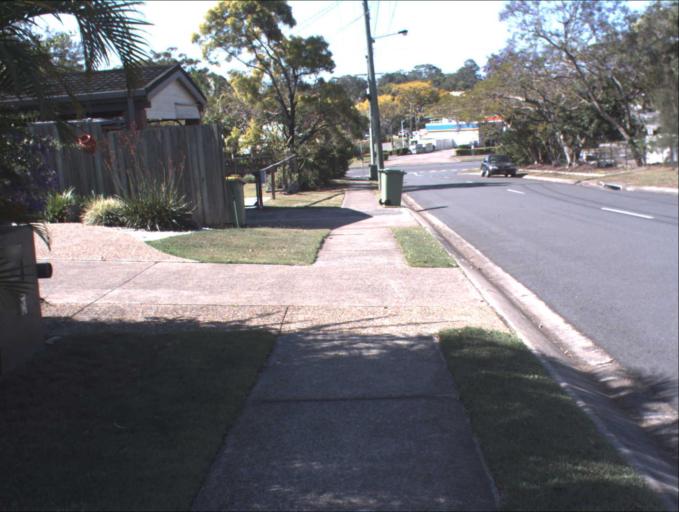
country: AU
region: Queensland
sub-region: Logan
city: Rochedale South
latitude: -27.5962
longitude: 153.1210
